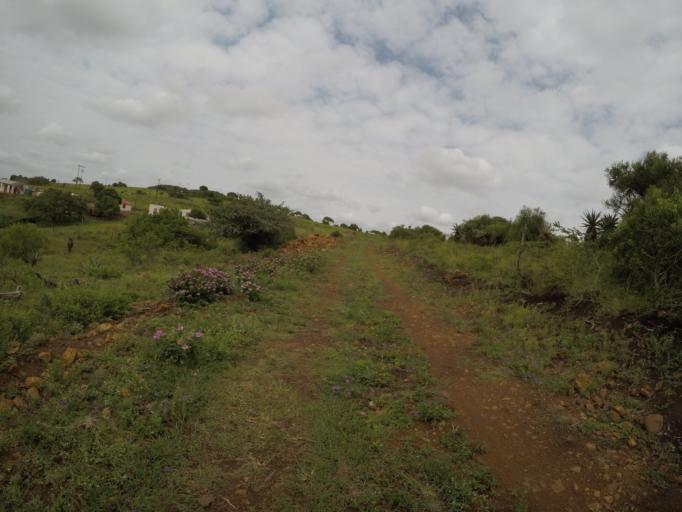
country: ZA
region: KwaZulu-Natal
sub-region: uThungulu District Municipality
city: Empangeni
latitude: -28.6134
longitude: 31.9004
